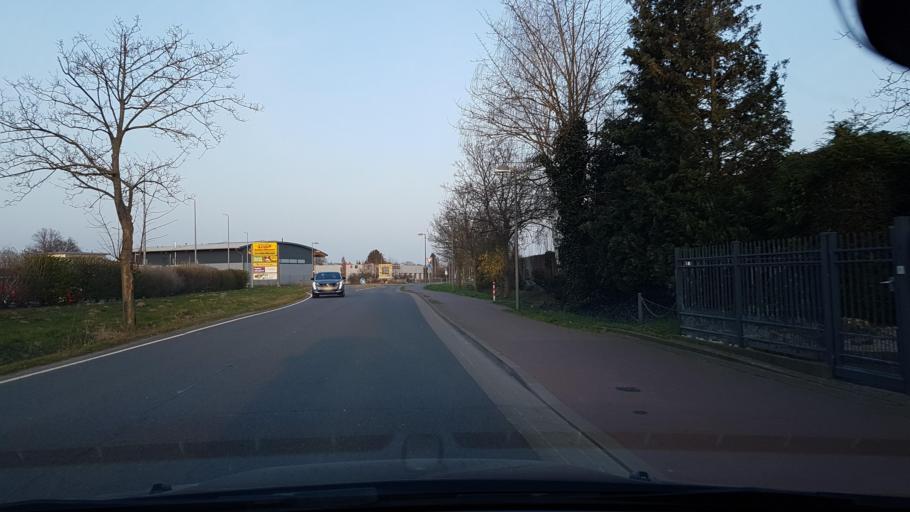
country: DE
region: Lower Saxony
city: Garbsen-Mitte
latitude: 52.4403
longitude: 9.5807
